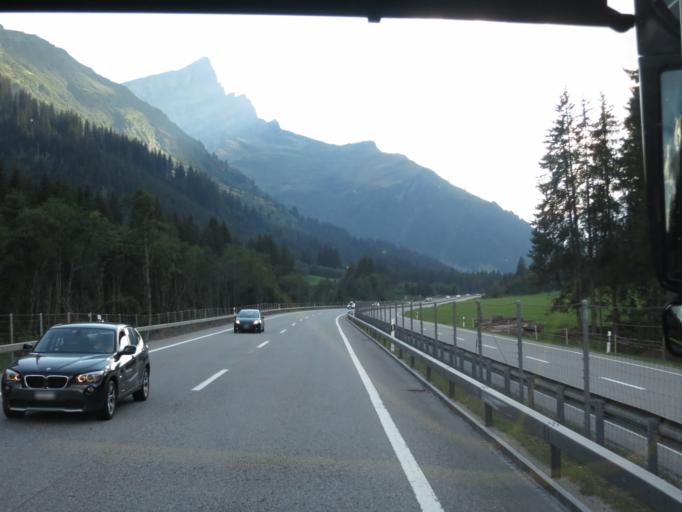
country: CH
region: Grisons
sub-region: Hinterrhein District
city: Hinterrhein
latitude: 46.5429
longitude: 9.2796
